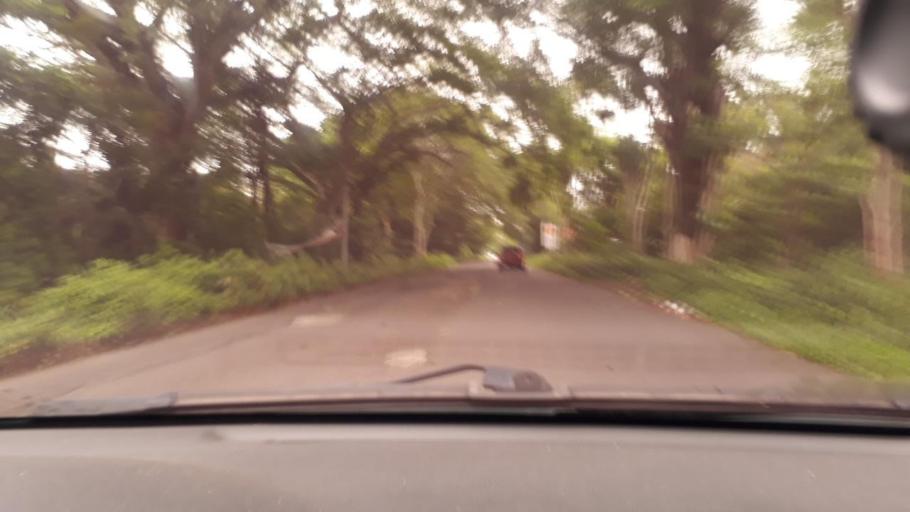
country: GT
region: Jutiapa
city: Jalpatagua
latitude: 14.1443
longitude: -90.0272
